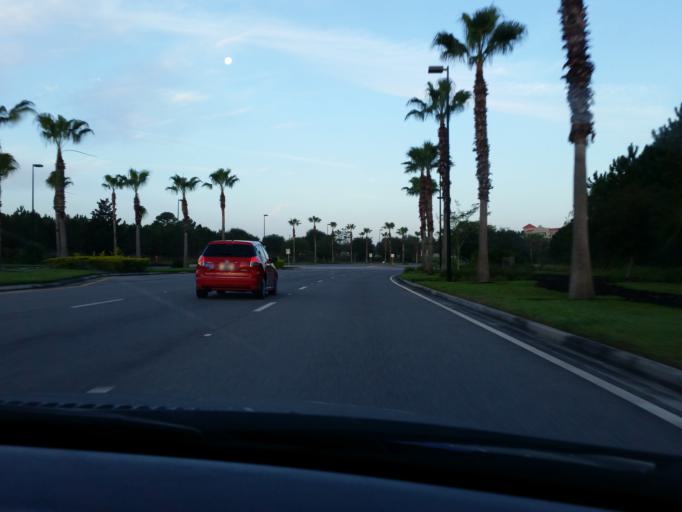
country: US
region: Florida
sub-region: Orange County
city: Tangelo Park
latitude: 28.4338
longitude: -81.4645
